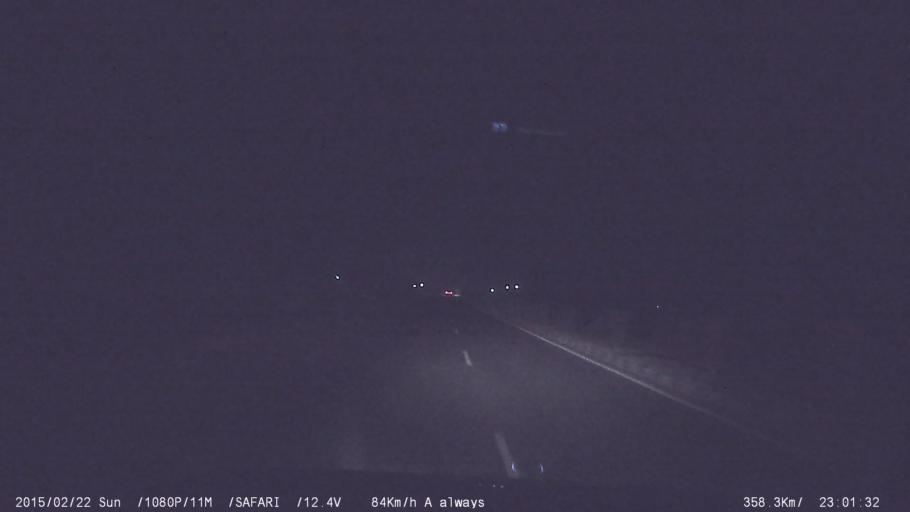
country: IN
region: Tamil Nadu
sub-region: Namakkal
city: Rasipuram
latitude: 11.3643
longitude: 78.1644
